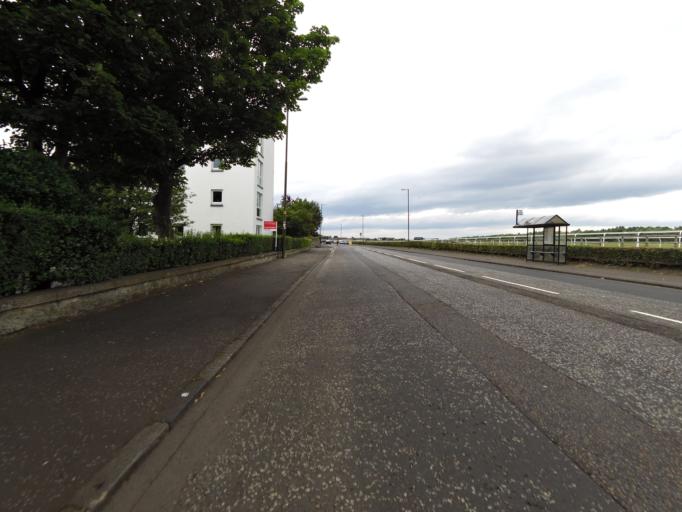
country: GB
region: Scotland
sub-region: East Lothian
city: Musselburgh
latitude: 55.9452
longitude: -3.0330
